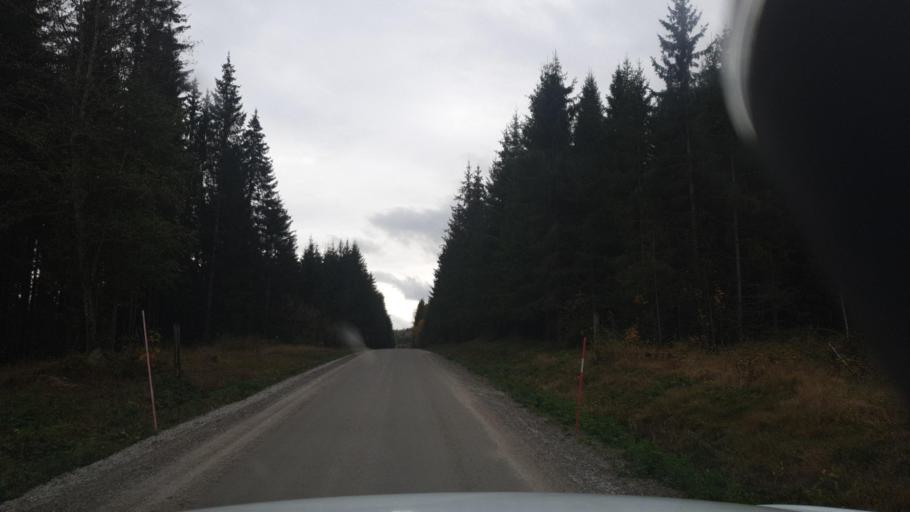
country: SE
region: Vaermland
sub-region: Arvika Kommun
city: Arvika
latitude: 59.7999
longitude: 12.7497
